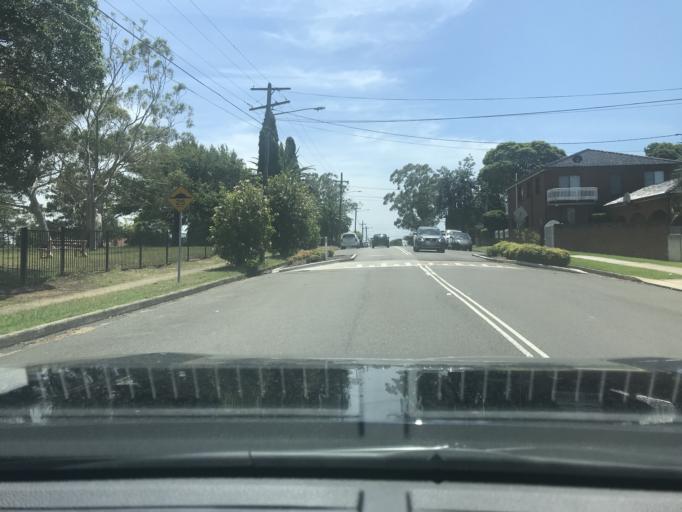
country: AU
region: New South Wales
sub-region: Canada Bay
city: Concord
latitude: -33.8605
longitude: 151.0998
